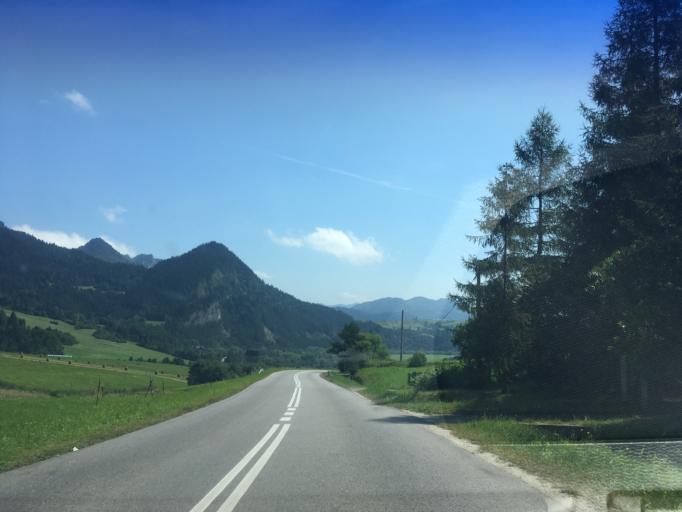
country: PL
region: Lesser Poland Voivodeship
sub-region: Powiat nowotarski
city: Krosnica
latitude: 49.4086
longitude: 20.3548
